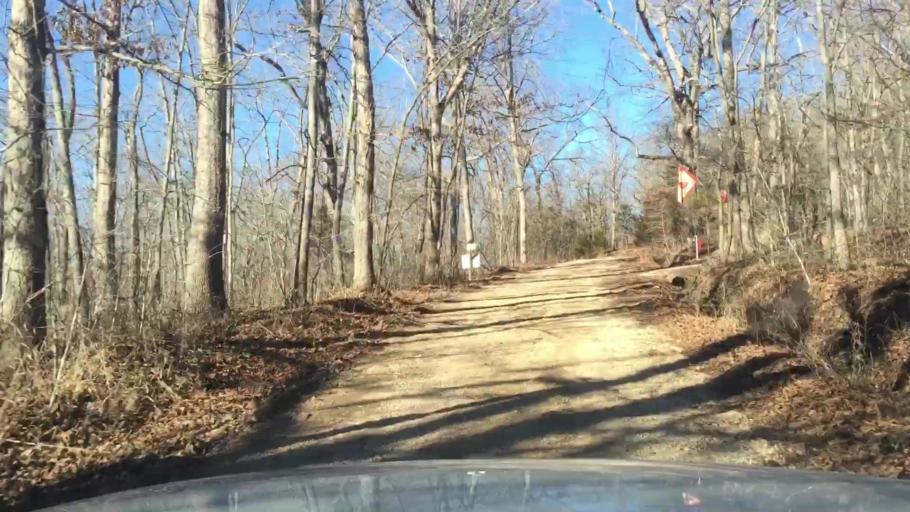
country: US
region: Missouri
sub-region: Morgan County
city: Versailles
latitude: 38.3225
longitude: -92.7641
